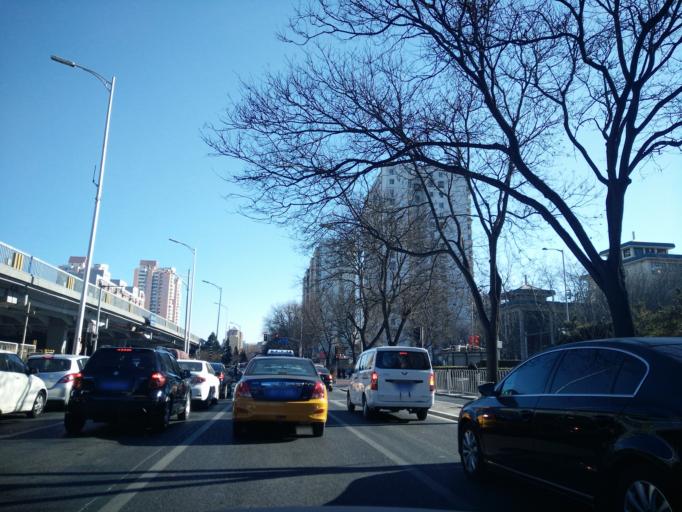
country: CN
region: Beijing
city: Dahongmen
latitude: 39.8555
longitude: 116.4073
